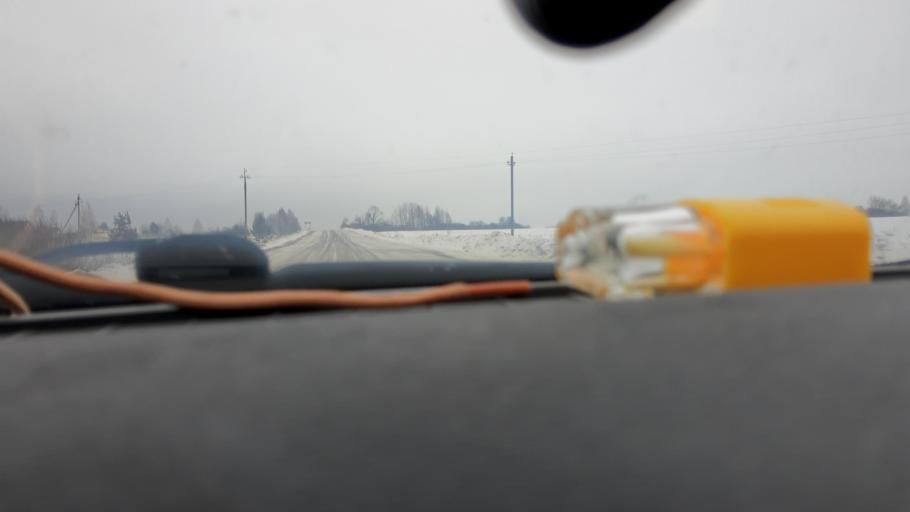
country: RU
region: Bashkortostan
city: Iglino
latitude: 54.6334
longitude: 56.4249
